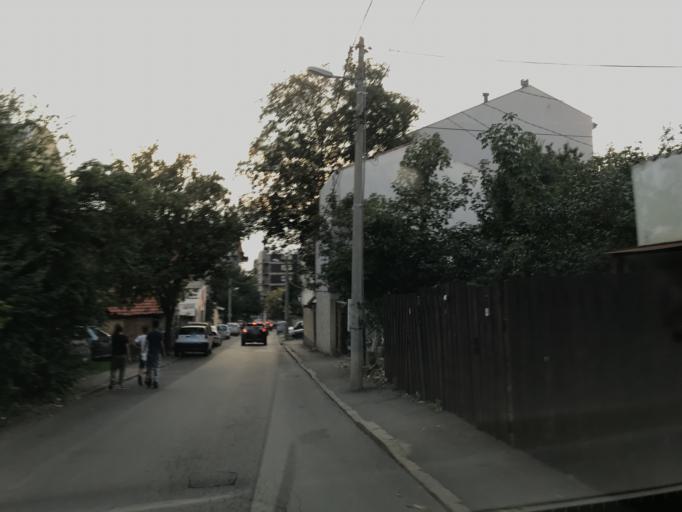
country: RS
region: Central Serbia
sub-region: Belgrade
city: Palilula
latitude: 44.7882
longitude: 20.5104
